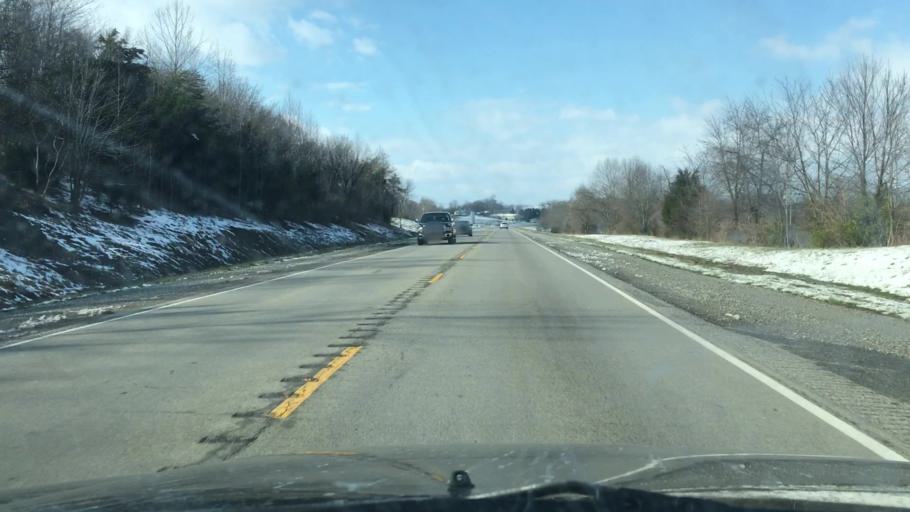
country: US
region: Kentucky
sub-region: Marion County
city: Lebanon
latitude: 37.5298
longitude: -85.3034
